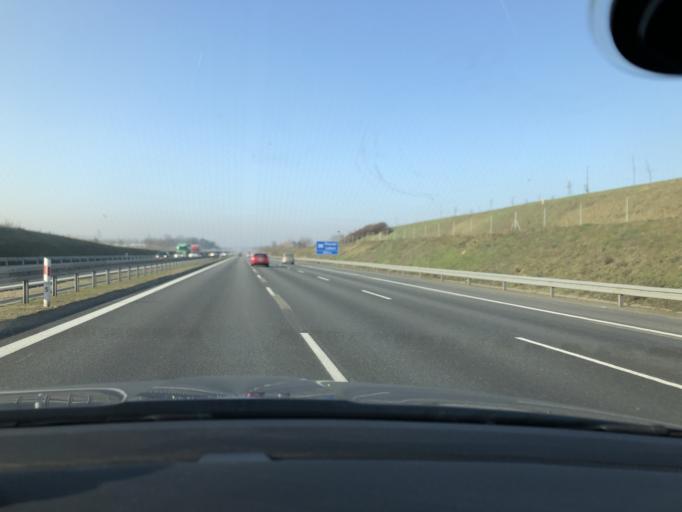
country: PL
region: Greater Poland Voivodeship
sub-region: Powiat poznanski
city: Daszewice
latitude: 52.3493
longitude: 16.9559
